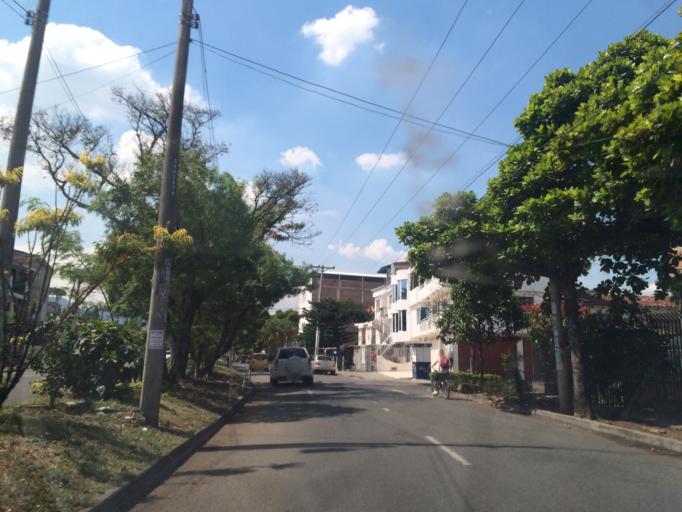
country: CO
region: Valle del Cauca
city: Cali
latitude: 3.4150
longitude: -76.5243
